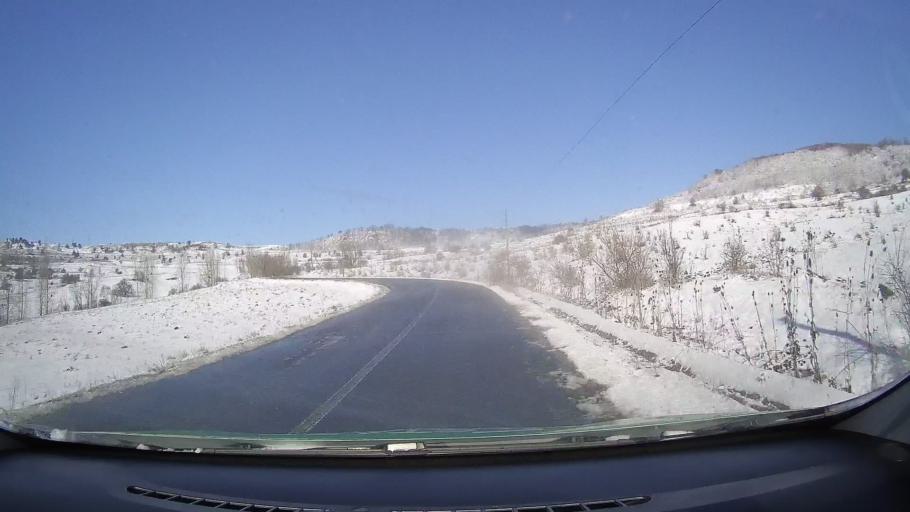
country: RO
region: Sibiu
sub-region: Comuna Avrig
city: Avrig
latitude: 45.7721
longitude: 24.3839
